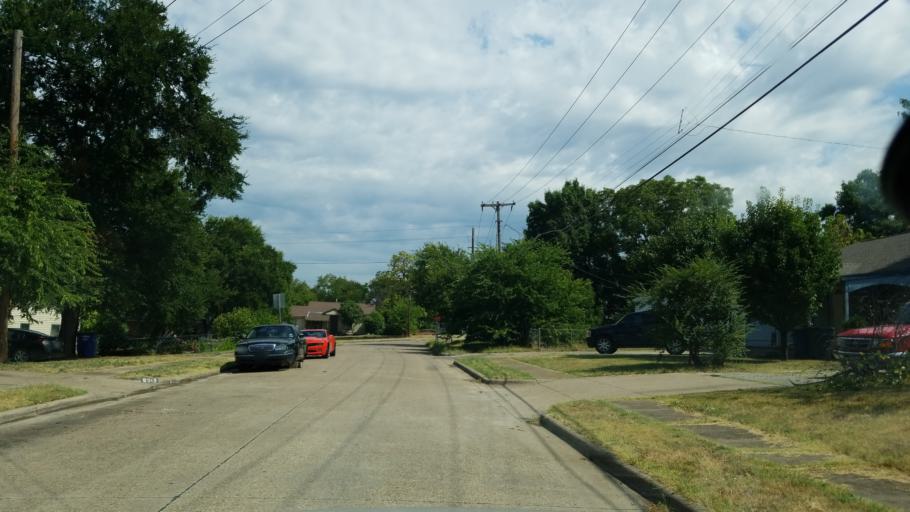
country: US
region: Texas
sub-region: Dallas County
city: Duncanville
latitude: 32.6685
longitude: -96.8349
